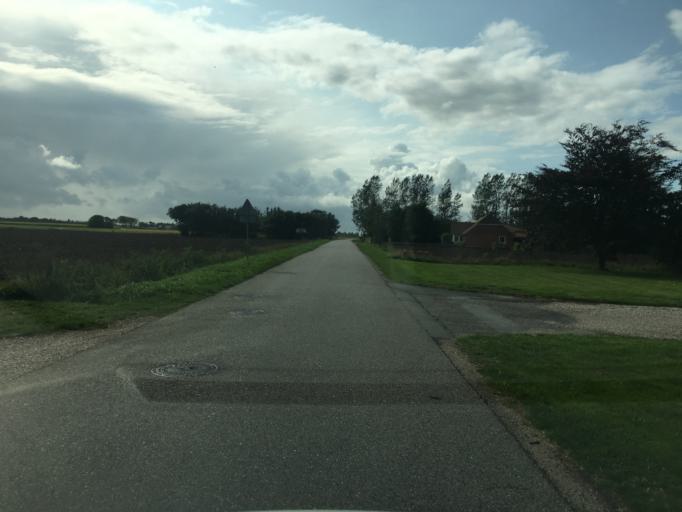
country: DK
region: South Denmark
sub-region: Tonder Kommune
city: Tonder
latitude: 54.9781
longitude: 8.8602
